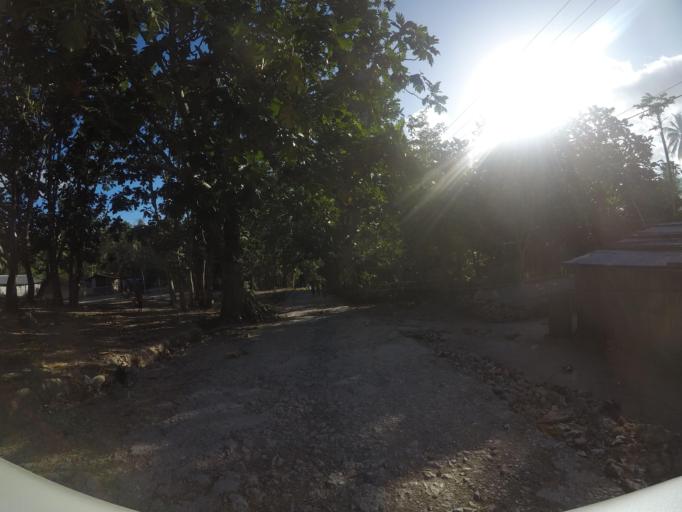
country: TL
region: Lautem
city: Lospalos
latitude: -8.4390
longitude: 126.8567
